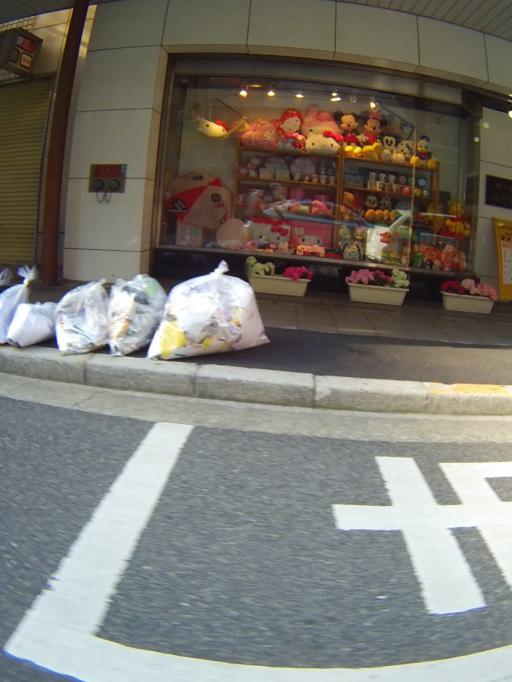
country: JP
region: Osaka
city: Osaka-shi
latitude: 34.6792
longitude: 135.5080
